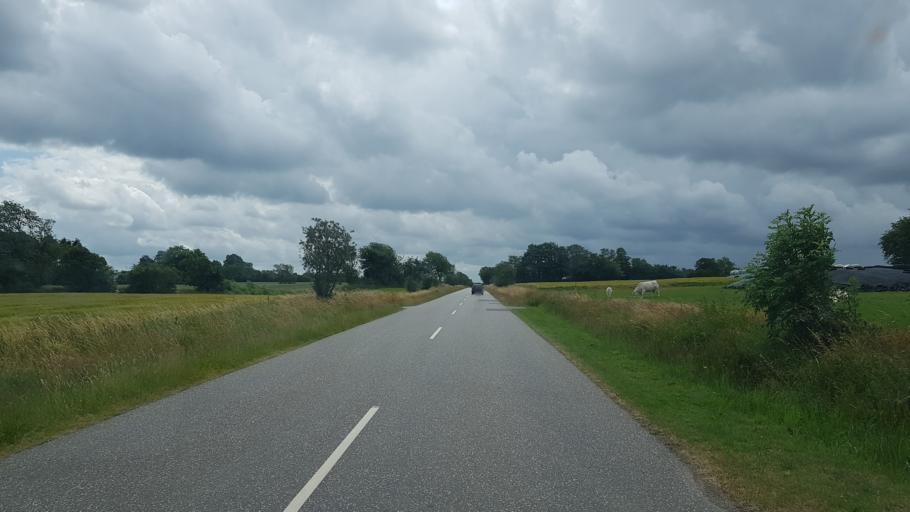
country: DK
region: South Denmark
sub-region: Kolding Kommune
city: Vamdrup
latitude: 55.4498
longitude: 9.2739
